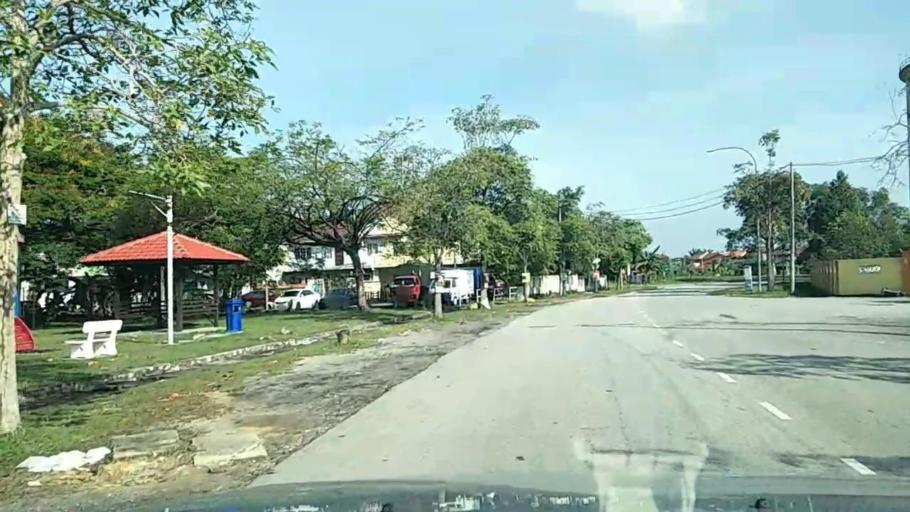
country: MY
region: Putrajaya
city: Putrajaya
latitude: 2.9400
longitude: 101.6199
